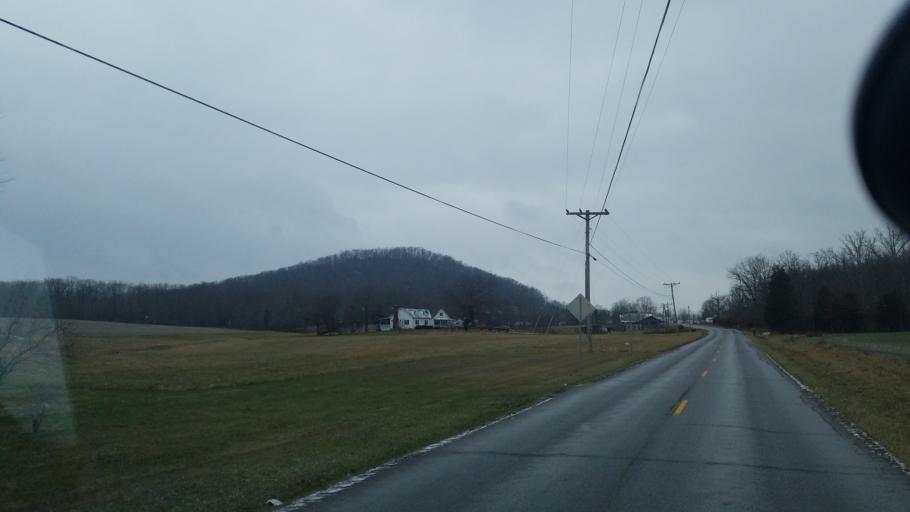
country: US
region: Kentucky
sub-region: Fleming County
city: Flemingsburg
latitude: 38.4763
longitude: -83.5976
